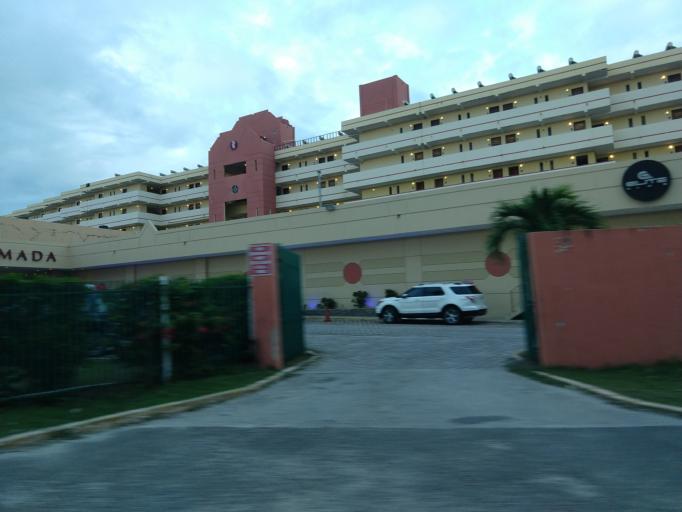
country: BZ
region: Belize
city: Belize City
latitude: 17.5047
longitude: -88.1886
